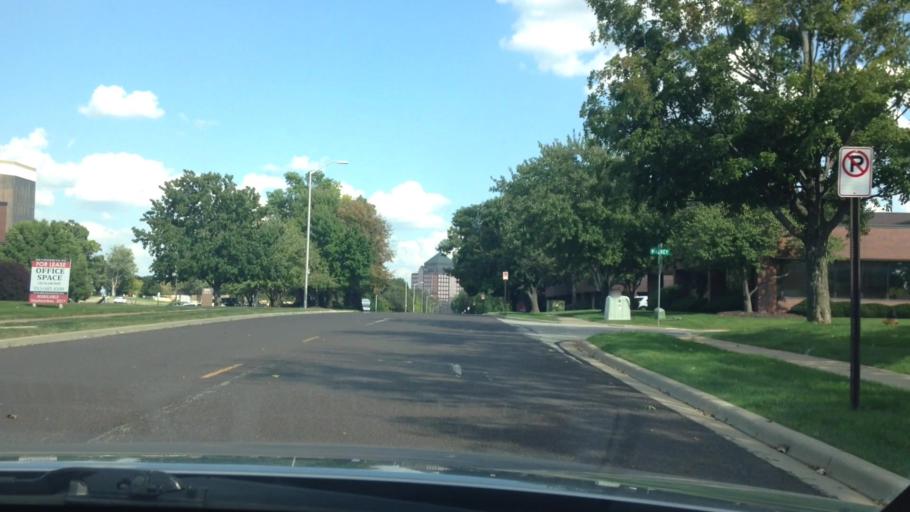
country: US
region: Kansas
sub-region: Johnson County
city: Overland Park
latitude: 38.9290
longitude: -94.6840
